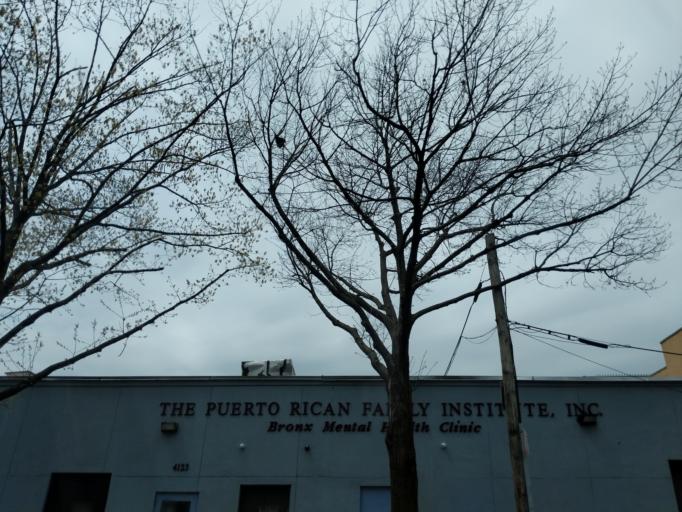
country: US
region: New York
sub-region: Bronx
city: The Bronx
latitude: 40.8448
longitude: -73.8971
